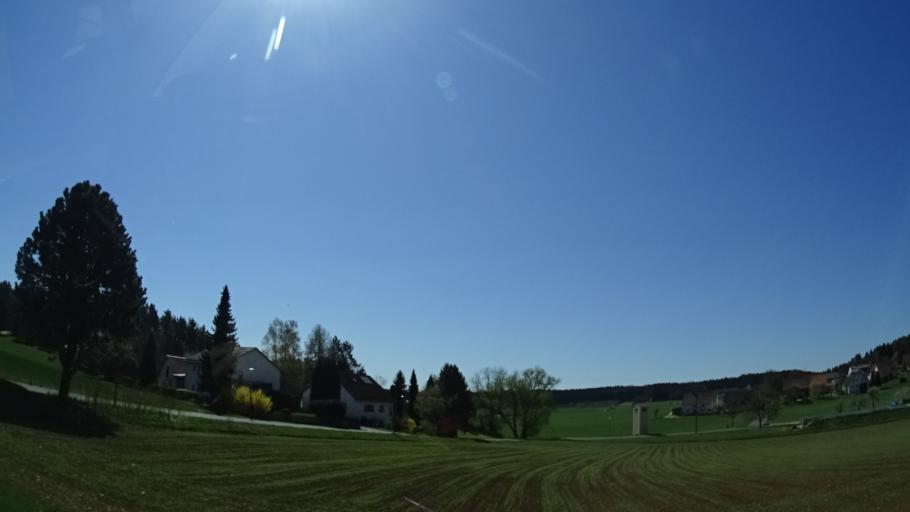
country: DE
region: Bavaria
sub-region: Upper Palatinate
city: Lauterhofen
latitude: 49.4073
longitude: 11.6216
